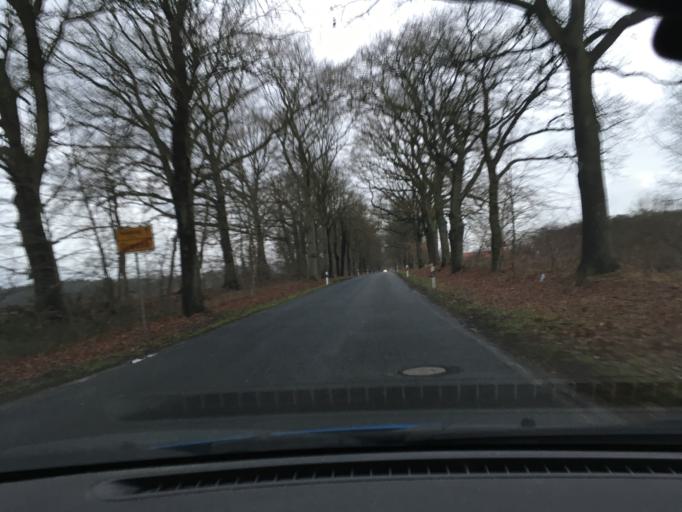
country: DE
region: Mecklenburg-Vorpommern
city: Boizenburg
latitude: 53.4294
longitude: 10.7386
